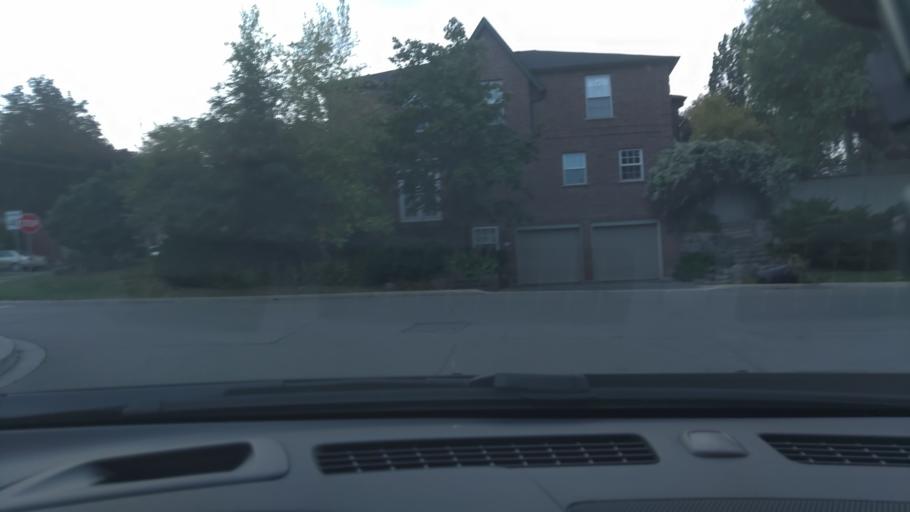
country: CA
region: Ontario
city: Toronto
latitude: 43.7195
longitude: -79.4217
